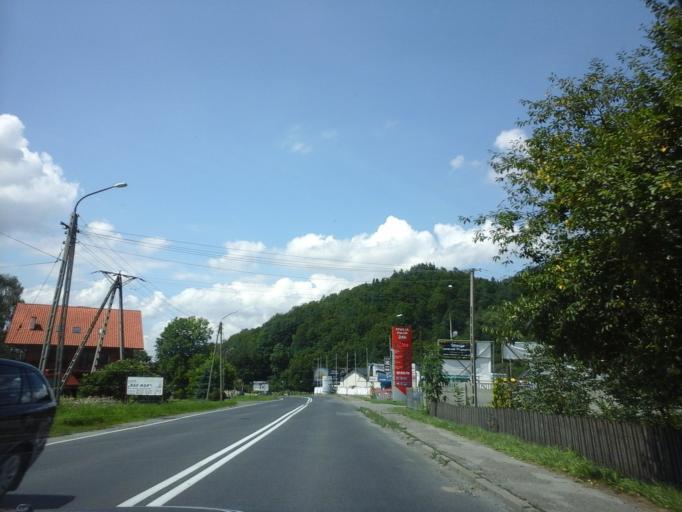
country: PL
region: Lesser Poland Voivodeship
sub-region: Powiat suski
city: Makow Podhalanski
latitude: 49.7321
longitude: 19.6610
